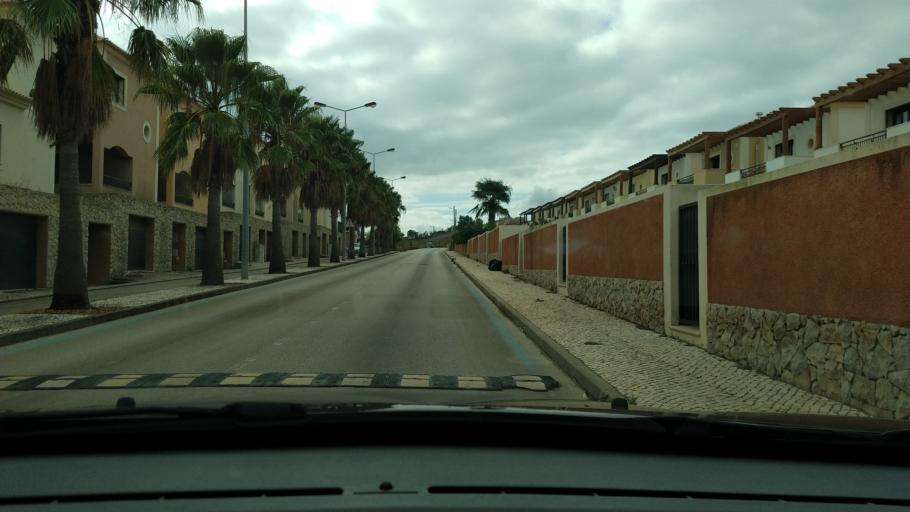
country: PT
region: Faro
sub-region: Lagos
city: Lagos
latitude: 37.0726
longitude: -8.7781
